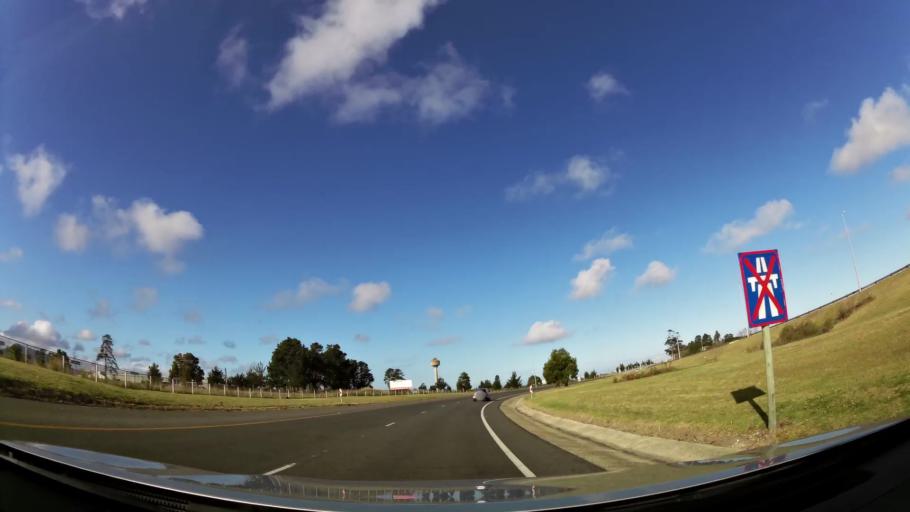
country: ZA
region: Western Cape
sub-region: Eden District Municipality
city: George
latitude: -33.9854
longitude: 22.5113
